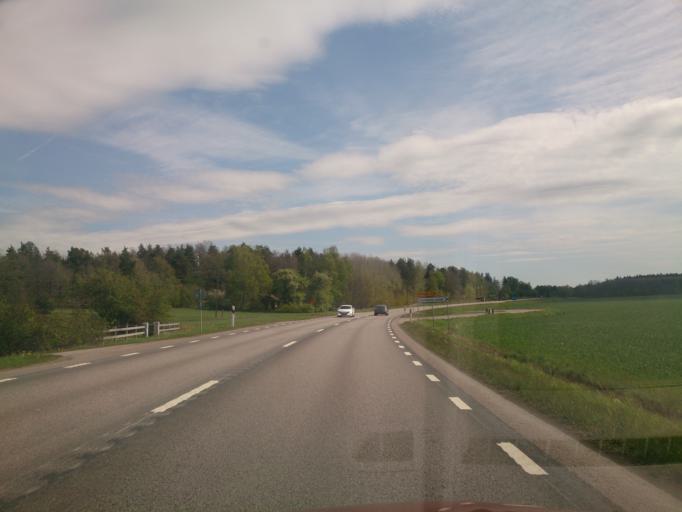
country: SE
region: OEstergoetland
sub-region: Linkopings Kommun
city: Sturefors
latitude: 58.4008
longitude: 15.7110
